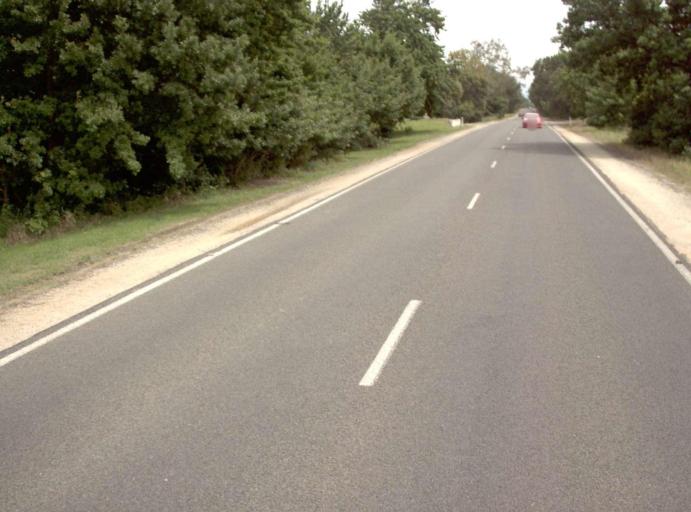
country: AU
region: Victoria
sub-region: Wellington
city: Sale
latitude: -38.0055
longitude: 147.0044
